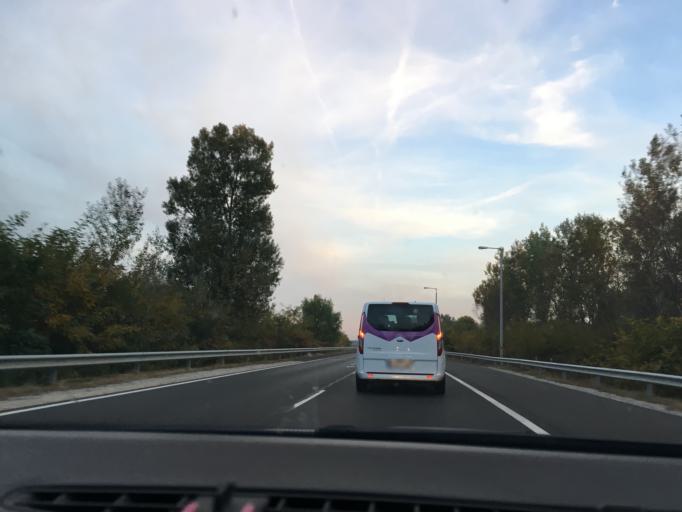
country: HU
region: Hajdu-Bihar
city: Hajduhadhaz
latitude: 47.6711
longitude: 21.6500
